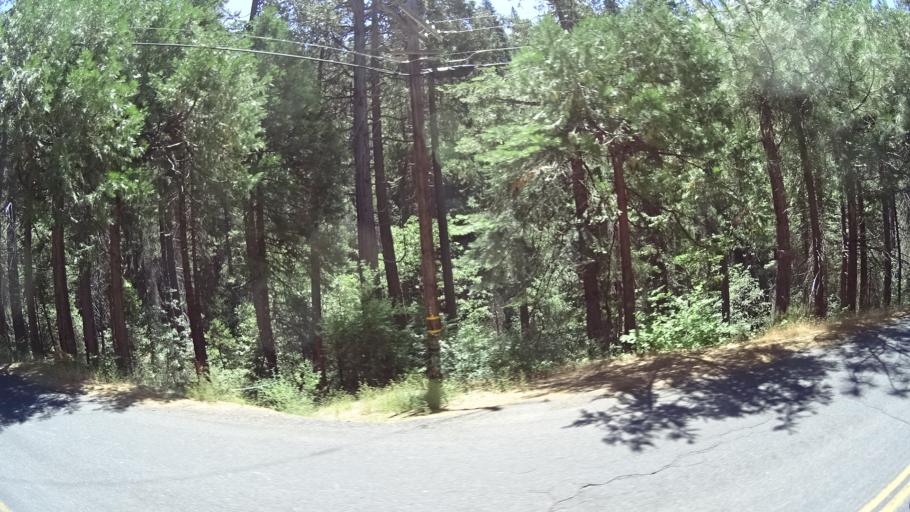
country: US
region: California
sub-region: Calaveras County
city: Arnold
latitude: 38.2320
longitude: -120.3532
